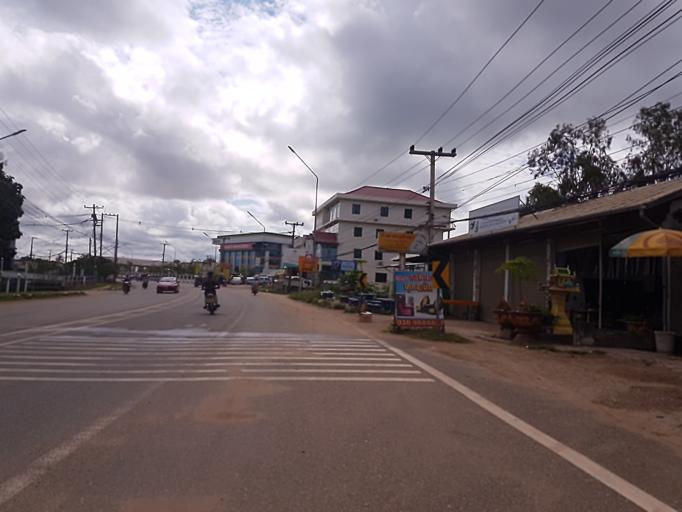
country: TH
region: Nong Khai
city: Tha Bo
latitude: 17.8708
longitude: 102.6543
